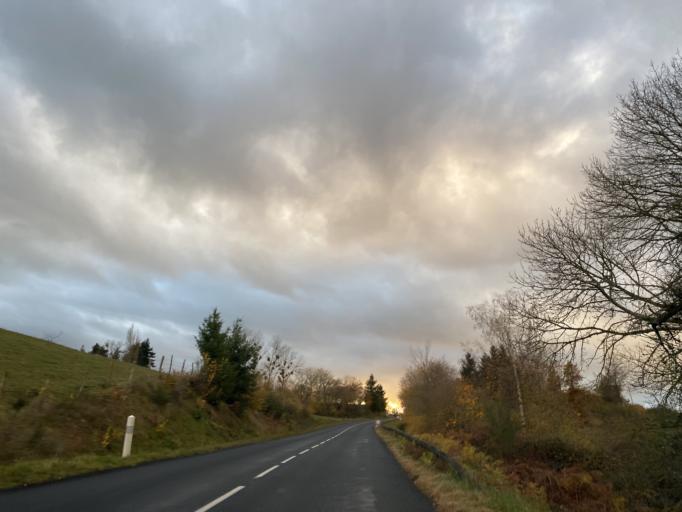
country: FR
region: Auvergne
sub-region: Departement du Puy-de-Dome
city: Cunlhat
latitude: 45.6966
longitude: 3.5815
